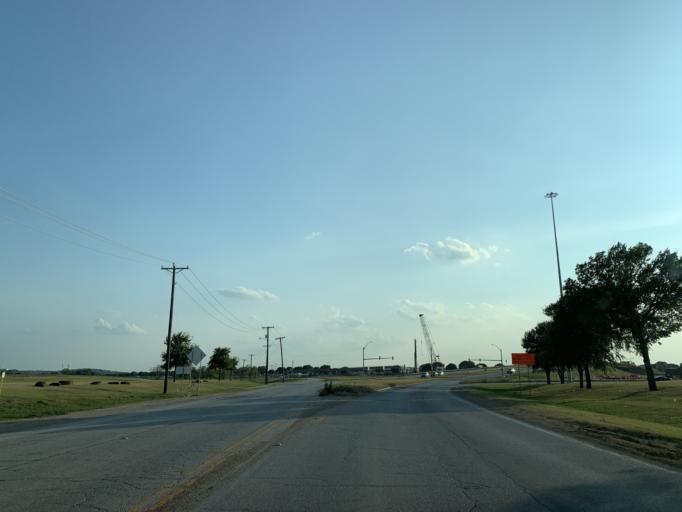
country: US
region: Texas
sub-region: Tarrant County
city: Richland Hills
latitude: 32.7988
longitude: -97.2085
